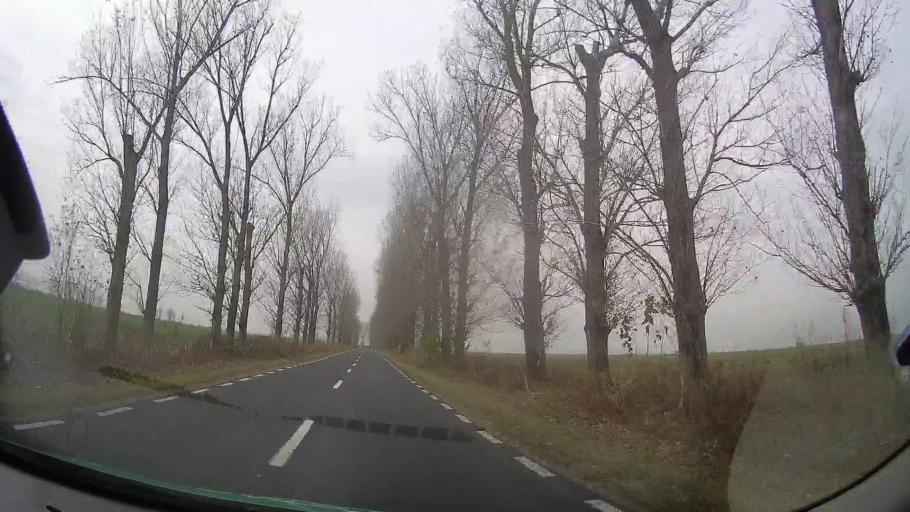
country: RO
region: Ilfov
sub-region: Comuna Gruiu
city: Lipia
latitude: 44.7228
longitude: 26.2781
